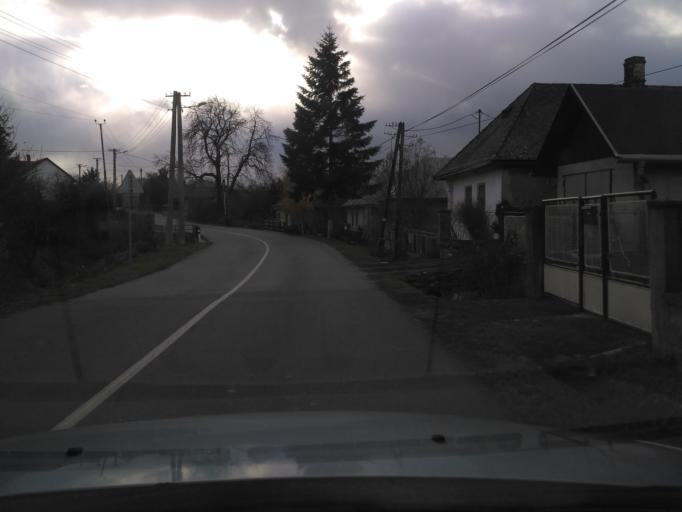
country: HU
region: Borsod-Abauj-Zemplen
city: Satoraljaujhely
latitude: 48.4219
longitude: 21.7280
